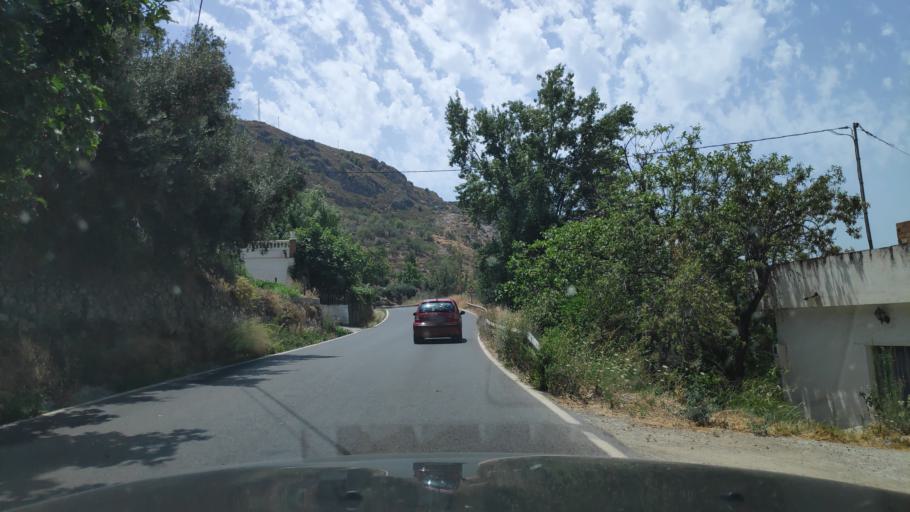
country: ES
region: Andalusia
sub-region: Provincia de Granada
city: Lanjaron
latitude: 36.9198
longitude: -3.4704
